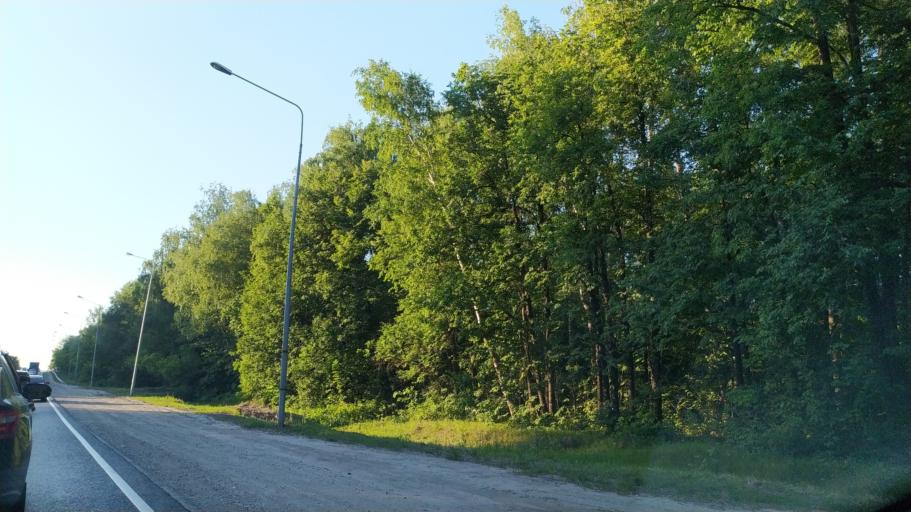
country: RU
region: Chuvashia
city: Kugesi
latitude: 56.0495
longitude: 47.2888
